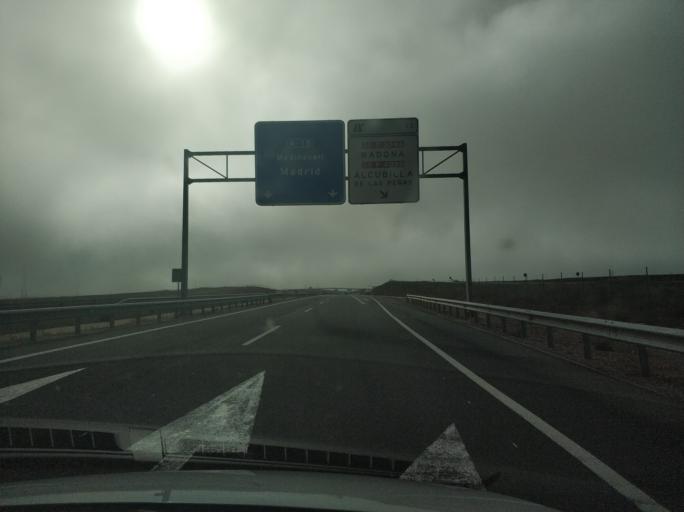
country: ES
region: Castille and Leon
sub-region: Provincia de Soria
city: Alcubilla de las Penas
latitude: 41.2671
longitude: -2.4744
